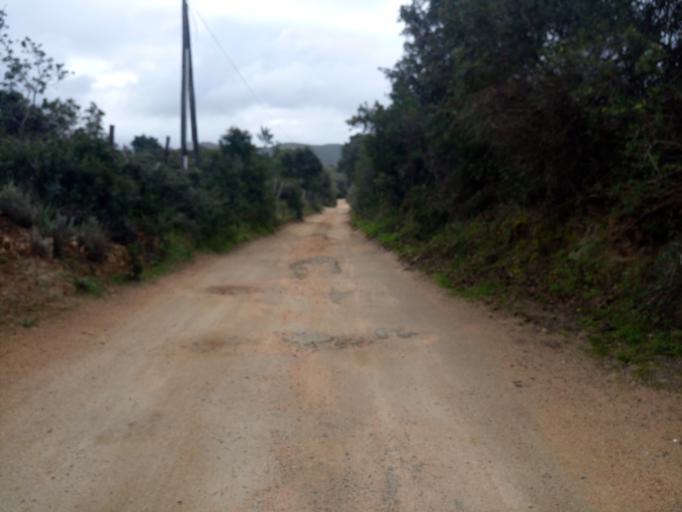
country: FR
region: Corsica
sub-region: Departement de la Corse-du-Sud
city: Sartene
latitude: 41.5488
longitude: 8.8904
